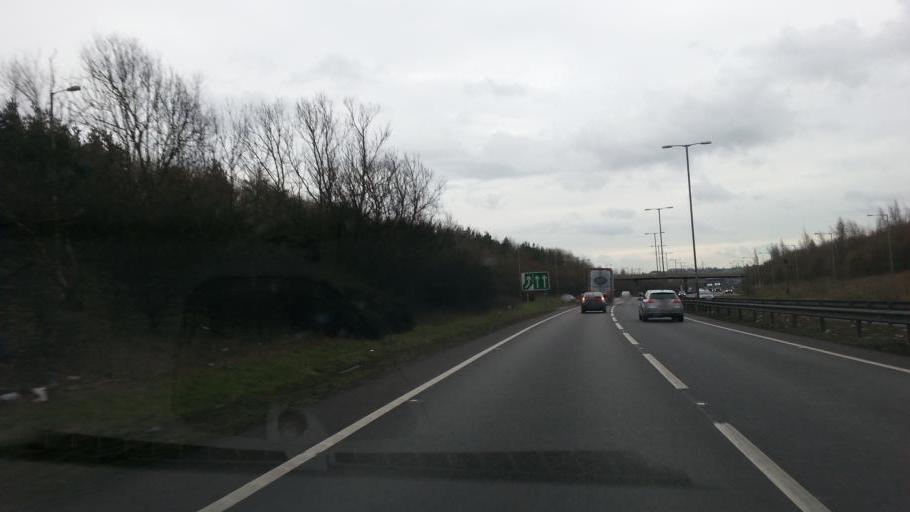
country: GB
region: England
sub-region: Northamptonshire
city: Kettering
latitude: 52.4054
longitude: -0.7521
